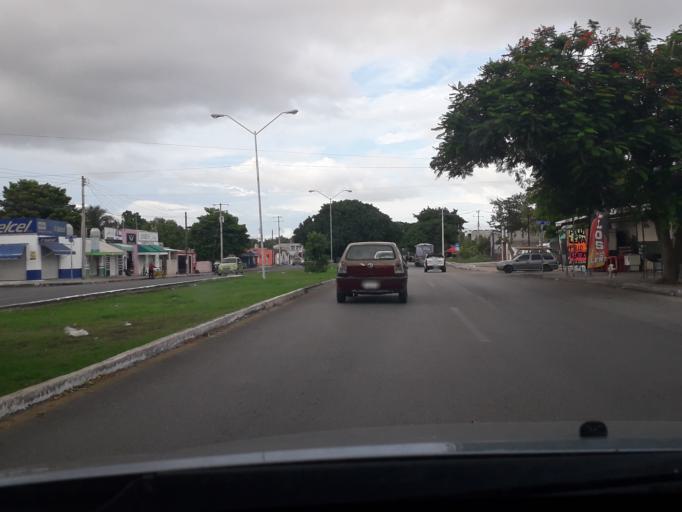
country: MX
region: Yucatan
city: Merida
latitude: 20.9619
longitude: -89.6633
